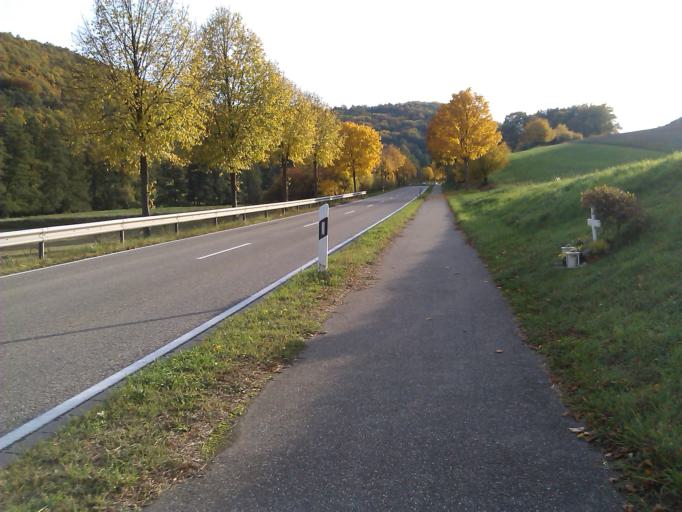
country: DE
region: Rheinland-Pfalz
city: Niederkirchen
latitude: 49.5696
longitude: 7.6933
